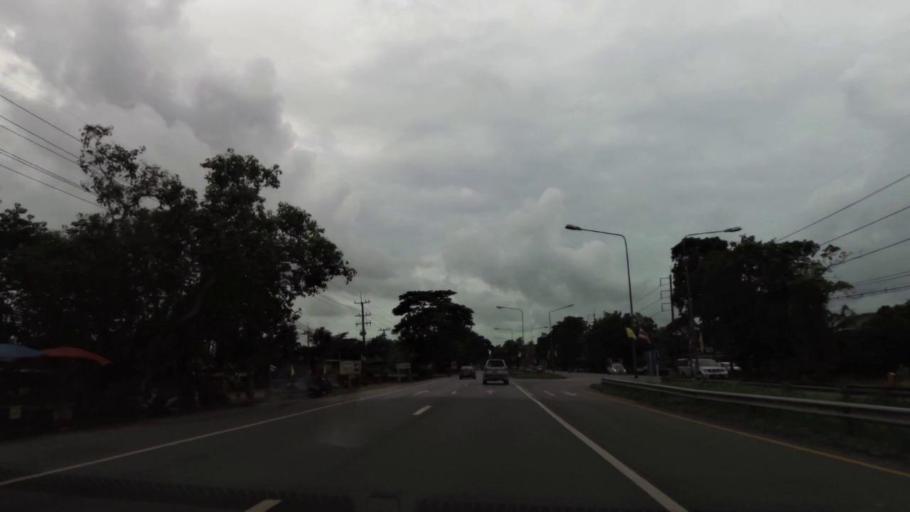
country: TH
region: Chanthaburi
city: Tha Mai
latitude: 12.6495
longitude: 102.0329
